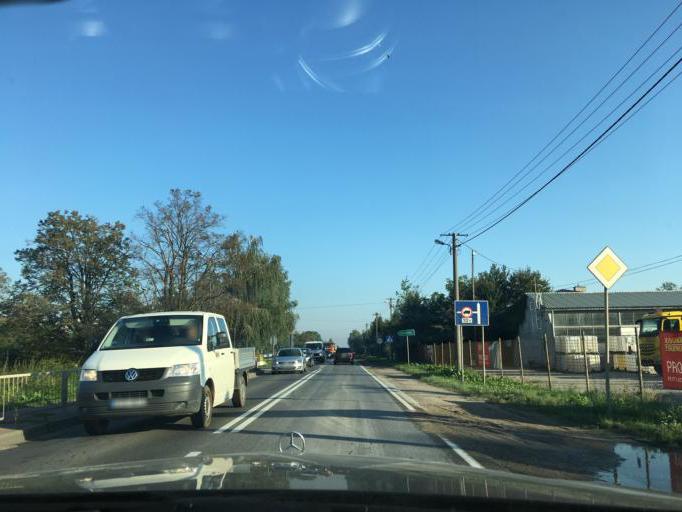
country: PL
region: Masovian Voivodeship
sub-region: Powiat grodziski
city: Grodzisk Mazowiecki
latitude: 52.1231
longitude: 20.6194
